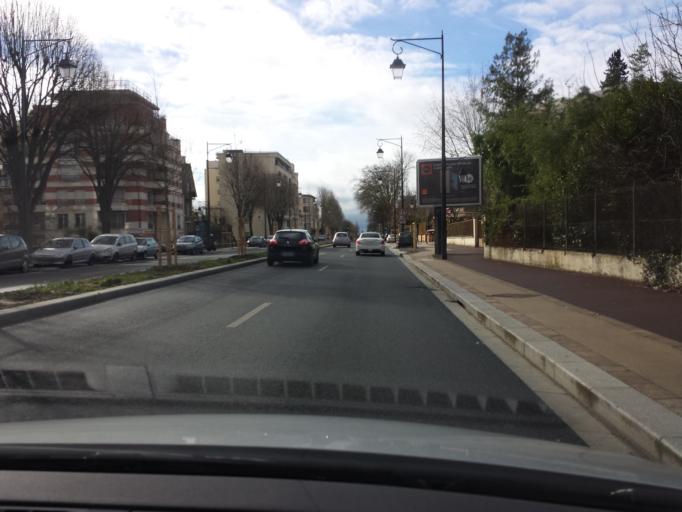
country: FR
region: Ile-de-France
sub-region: Departement des Hauts-de-Seine
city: Bourg-la-Reine
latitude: 48.7742
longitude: 2.3131
